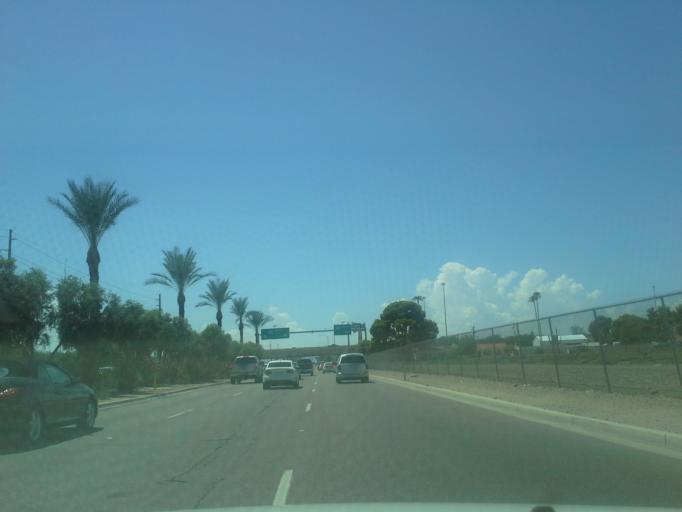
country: US
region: Arizona
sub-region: Maricopa County
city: Peoria
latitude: 33.5374
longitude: -112.2660
